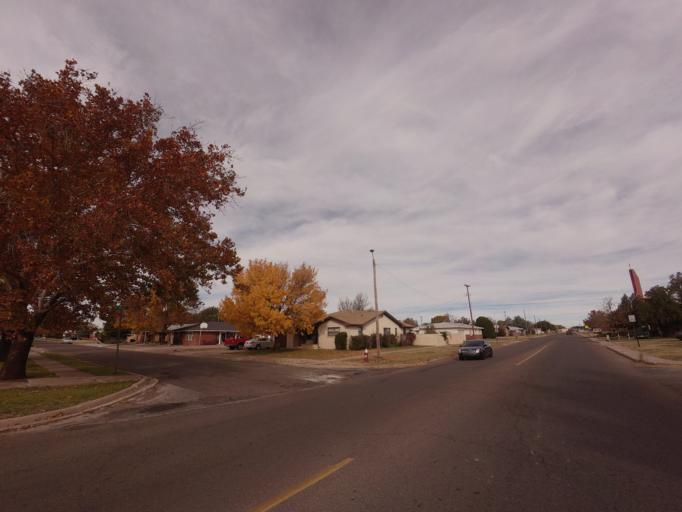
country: US
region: New Mexico
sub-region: Curry County
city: Clovis
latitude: 34.4229
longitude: -103.2070
